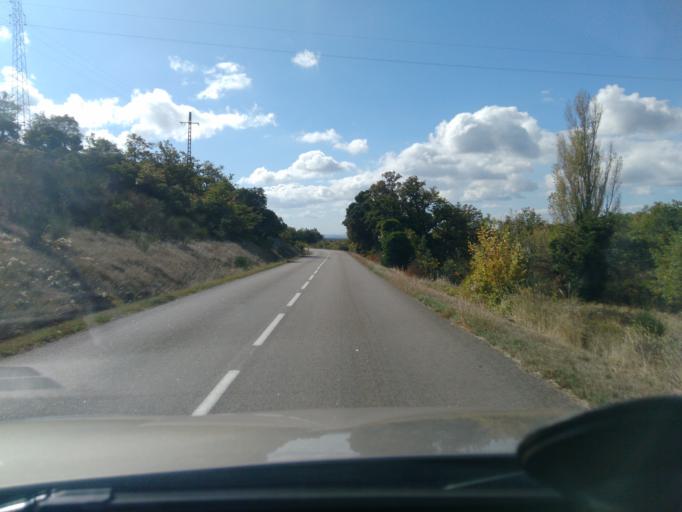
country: FR
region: Rhone-Alpes
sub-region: Departement de la Drome
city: Grignan
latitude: 44.4576
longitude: 4.9306
